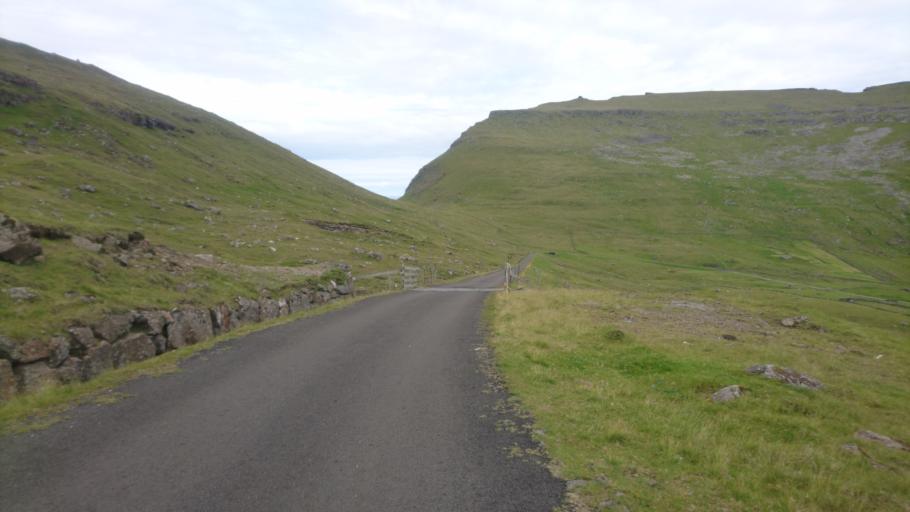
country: FO
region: Nordoyar
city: Klaksvik
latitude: 62.3312
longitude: -6.2871
